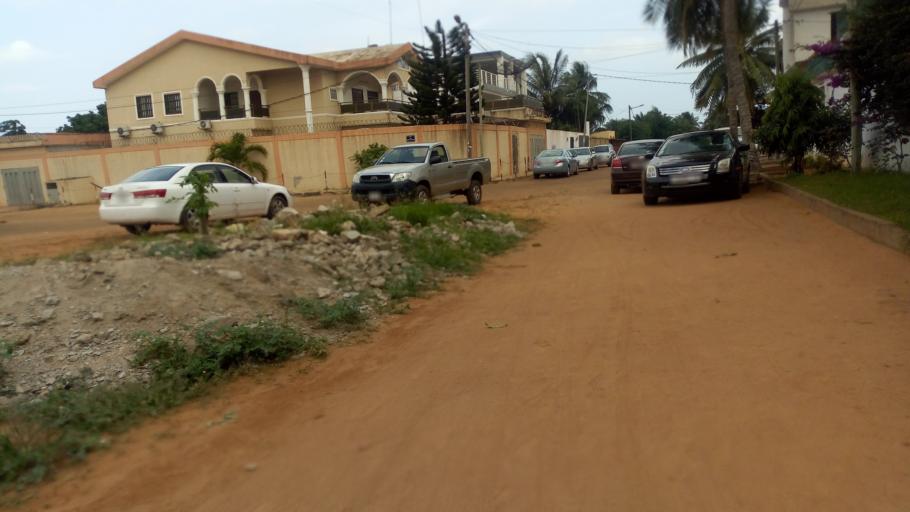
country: TG
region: Maritime
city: Lome
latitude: 6.1734
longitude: 1.1798
